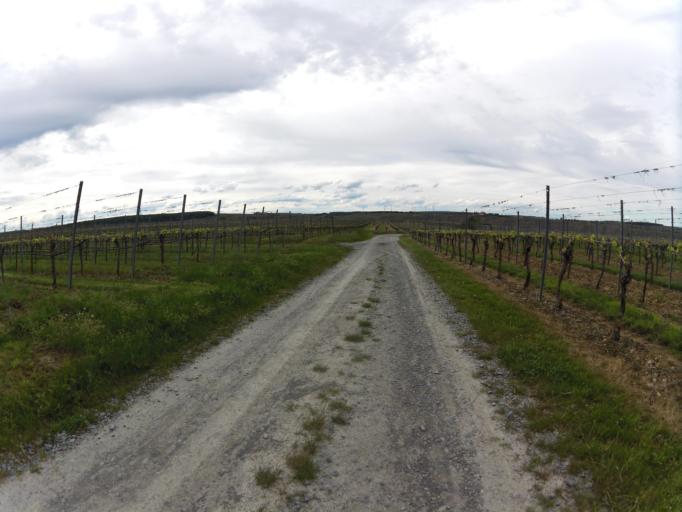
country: DE
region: Bavaria
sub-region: Regierungsbezirk Unterfranken
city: Nordheim
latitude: 49.8492
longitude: 10.1934
